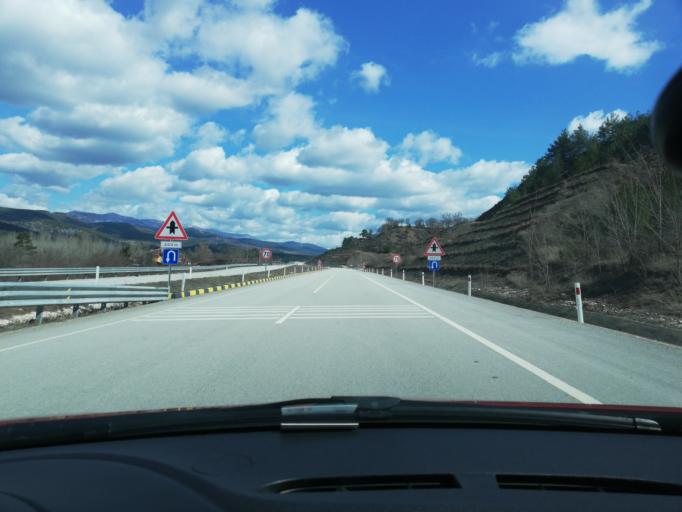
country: TR
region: Kastamonu
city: Igdir
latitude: 41.2316
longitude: 33.0424
